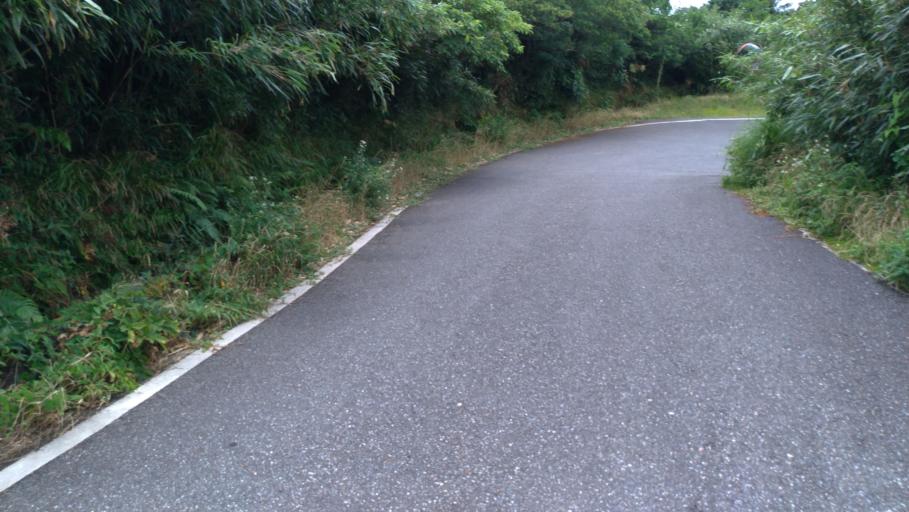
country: TW
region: Taipei
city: Taipei
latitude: 25.1822
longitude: 121.5229
